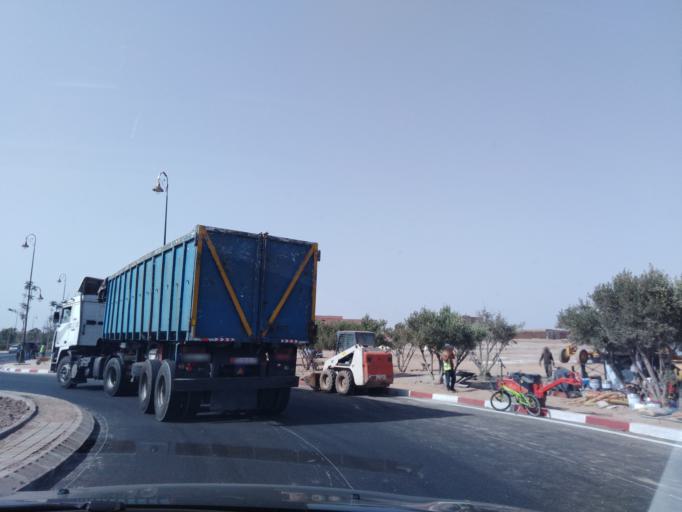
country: MA
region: Marrakech-Tensift-Al Haouz
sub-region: Kelaa-Des-Sraghna
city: Sidi Bou Othmane
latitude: 32.2238
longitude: -7.9570
